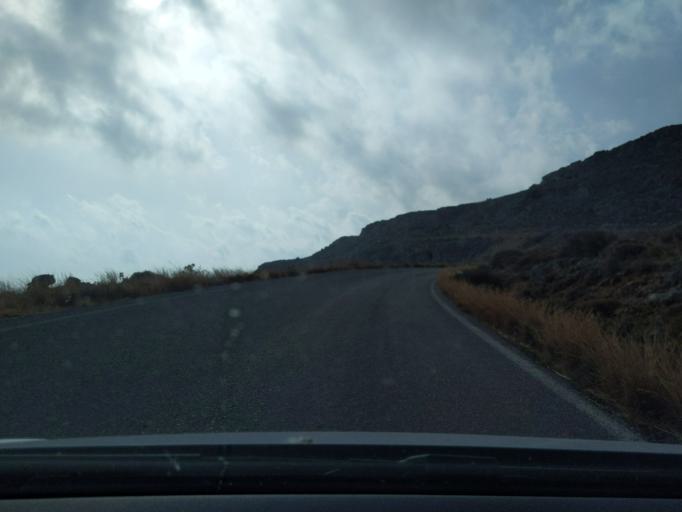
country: GR
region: Crete
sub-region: Nomos Lasithiou
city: Palekastro
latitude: 35.0931
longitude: 26.2631
